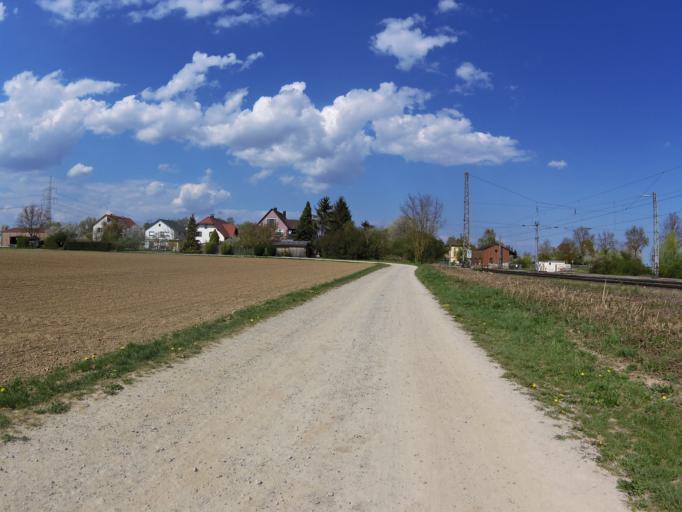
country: DE
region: Bavaria
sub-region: Regierungsbezirk Unterfranken
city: Oberpleichfeld
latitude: 49.8517
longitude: 10.1028
